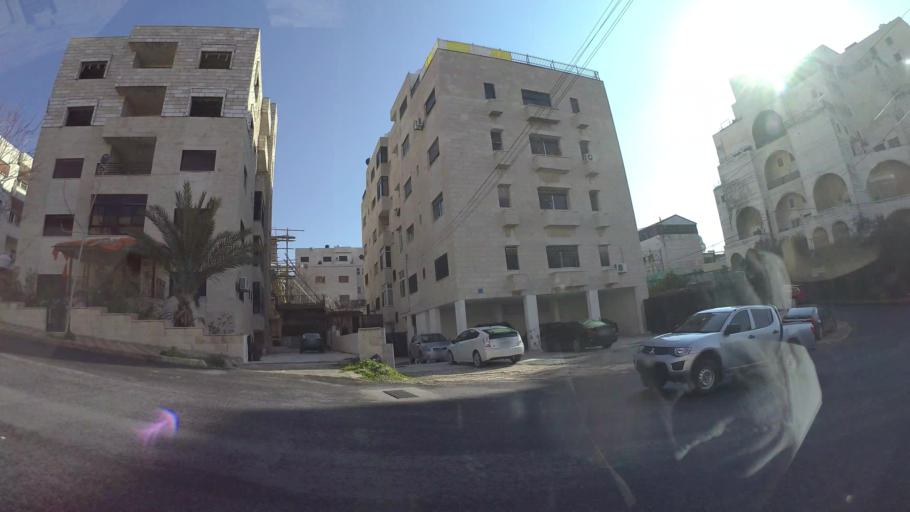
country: JO
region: Amman
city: Al Jubayhah
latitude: 31.9951
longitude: 35.8903
